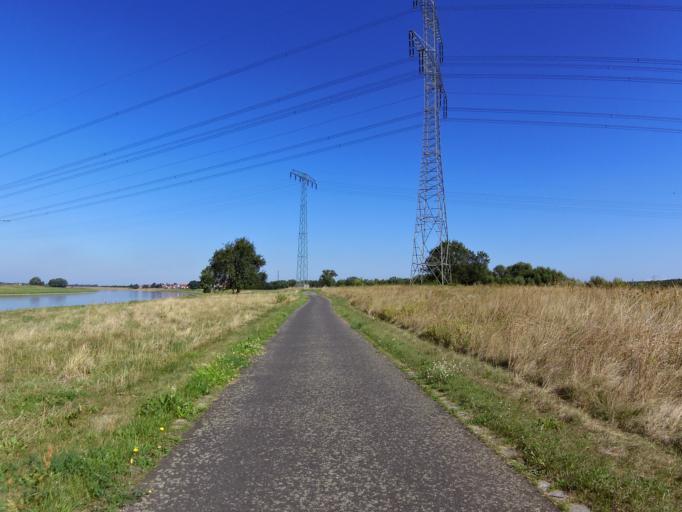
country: DE
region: Saxony
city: Riesa
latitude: 51.3367
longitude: 13.2938
